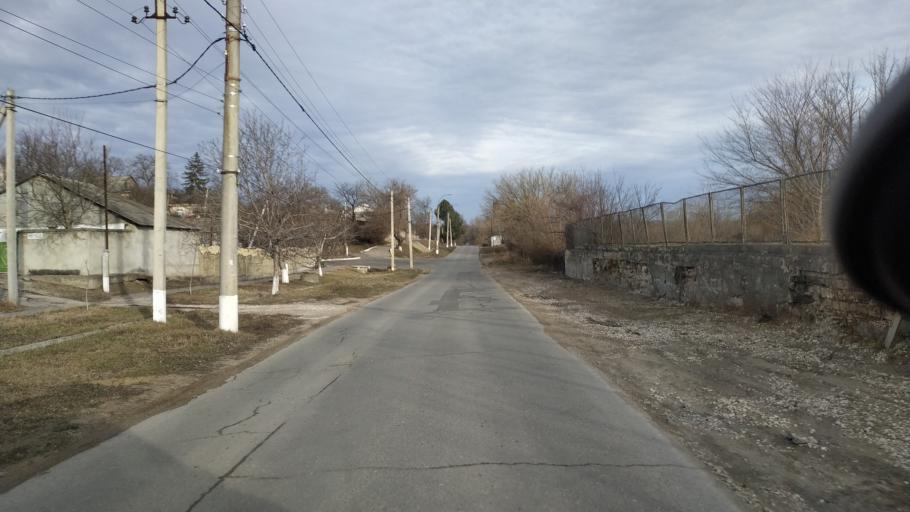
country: MD
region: Chisinau
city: Vadul lui Voda
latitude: 47.0969
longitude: 29.0709
